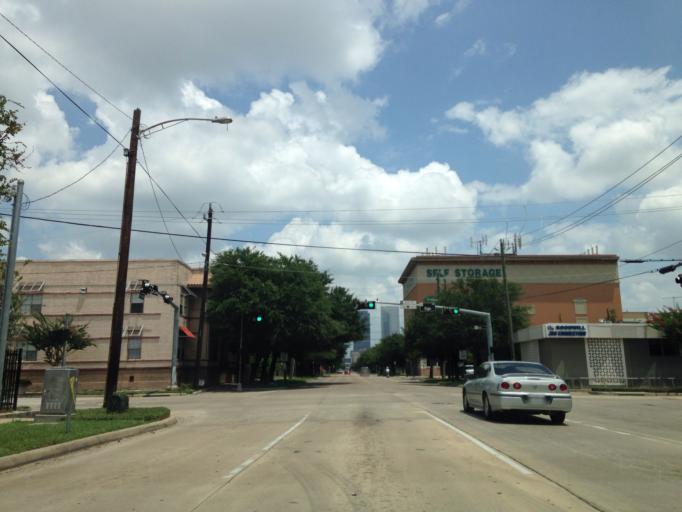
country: US
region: Texas
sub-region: Harris County
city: Houston
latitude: 29.7403
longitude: -95.3756
